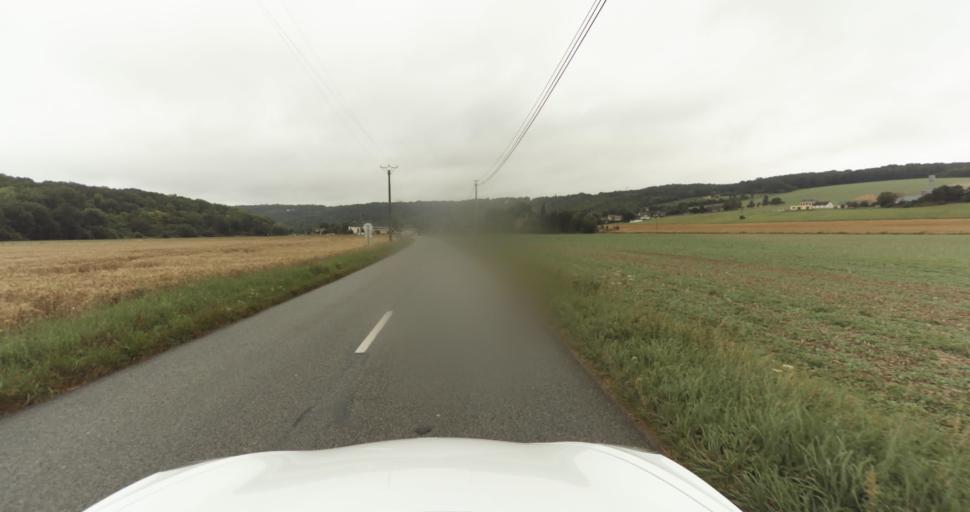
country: FR
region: Haute-Normandie
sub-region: Departement de l'Eure
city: Normanville
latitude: 49.0859
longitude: 1.1383
